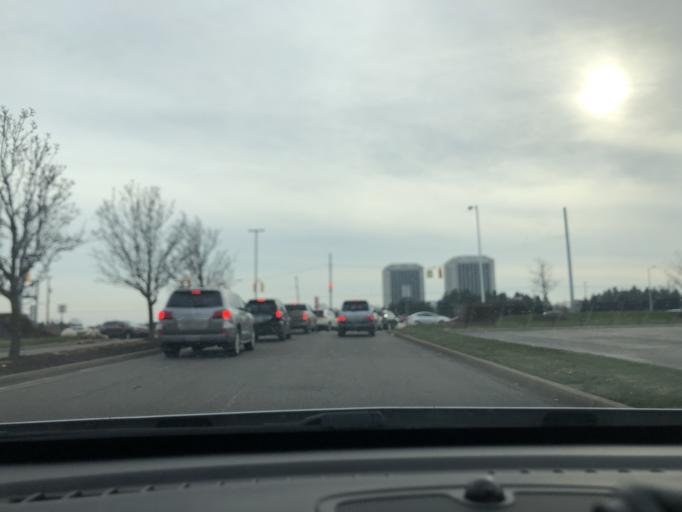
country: US
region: Michigan
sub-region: Wayne County
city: Dearborn
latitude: 42.3298
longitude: -83.2080
